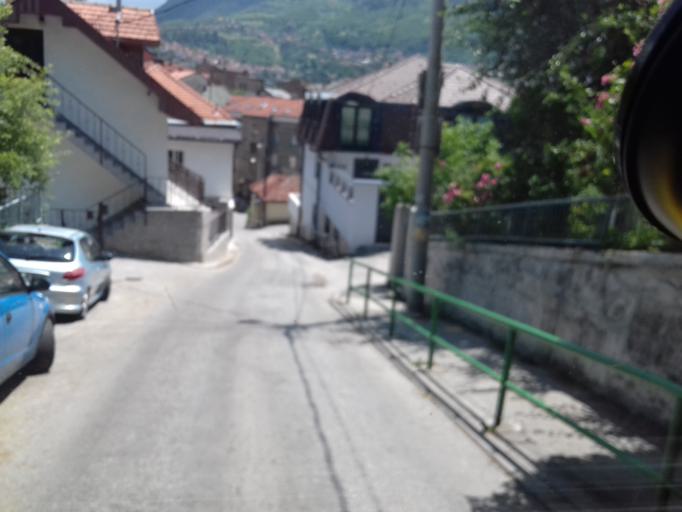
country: BA
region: Federation of Bosnia and Herzegovina
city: Kobilja Glava
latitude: 43.8638
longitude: 18.4247
